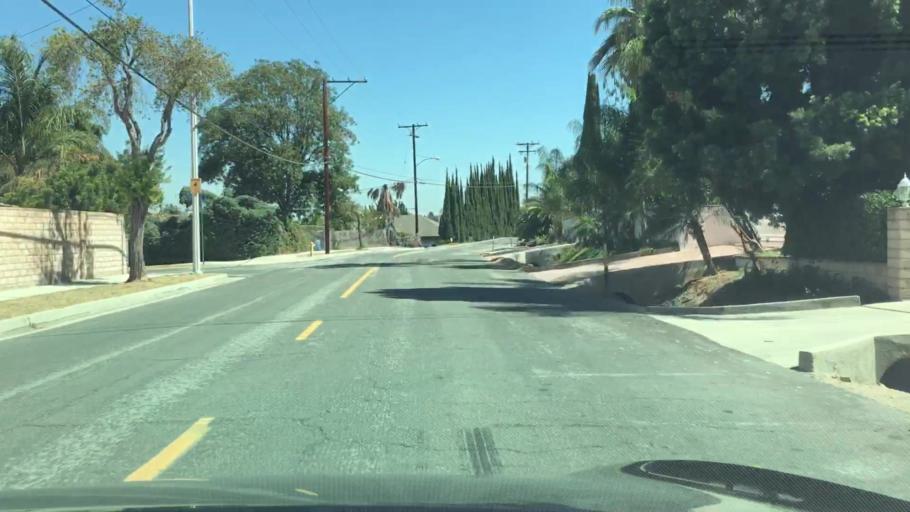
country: US
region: California
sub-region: Los Angeles County
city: Hacienda Heights
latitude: 34.0077
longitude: -117.9899
